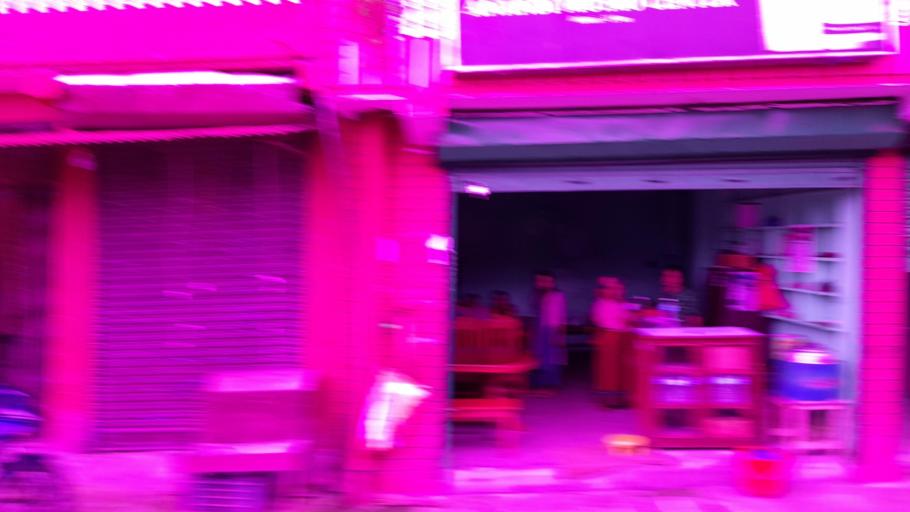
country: NP
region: Central Region
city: Kirtipur
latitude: 27.8282
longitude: 85.2095
